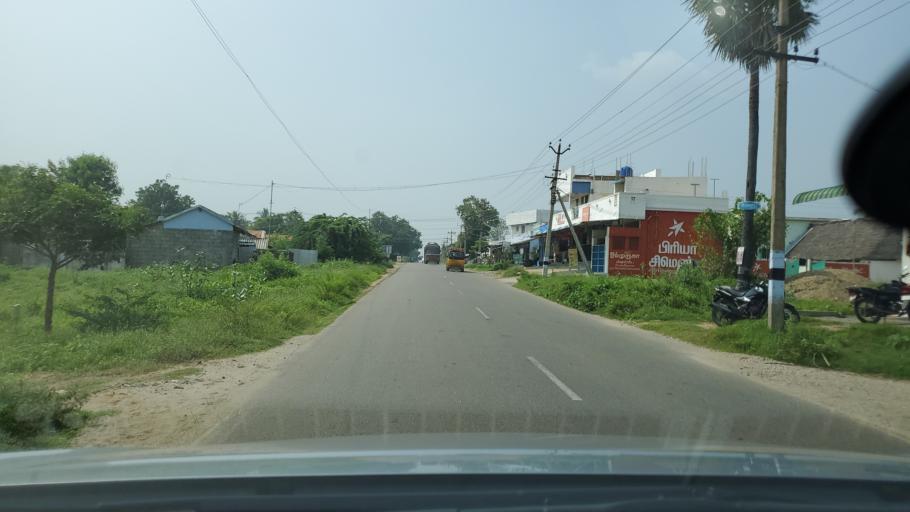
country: IN
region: Tamil Nadu
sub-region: Erode
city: Chennimalai
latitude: 11.1841
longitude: 77.6089
